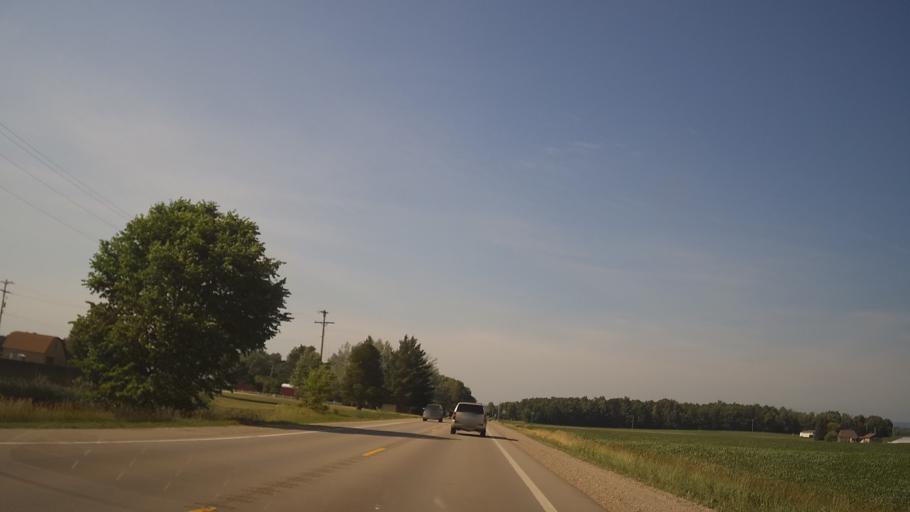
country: US
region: Michigan
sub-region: Ogemaw County
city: West Branch
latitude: 44.3085
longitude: -84.1258
